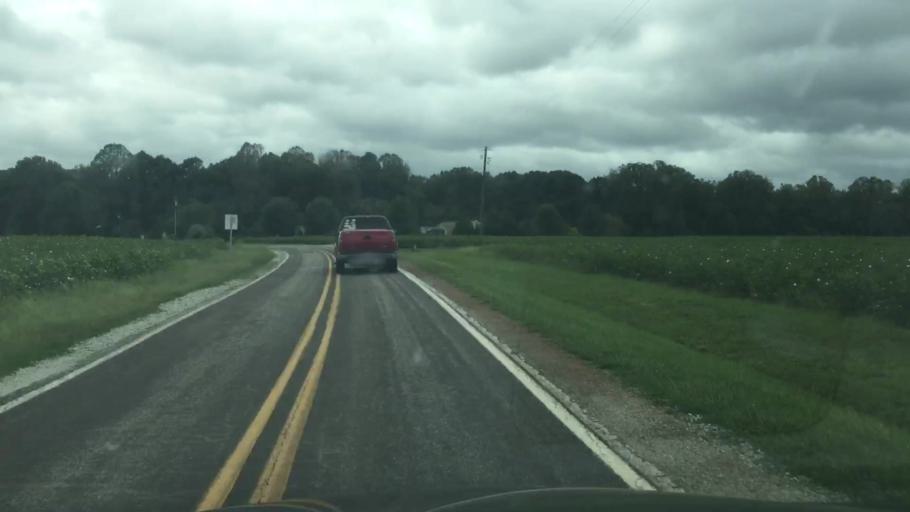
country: US
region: North Carolina
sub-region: Rowan County
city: China Grove
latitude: 35.6482
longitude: -80.6596
